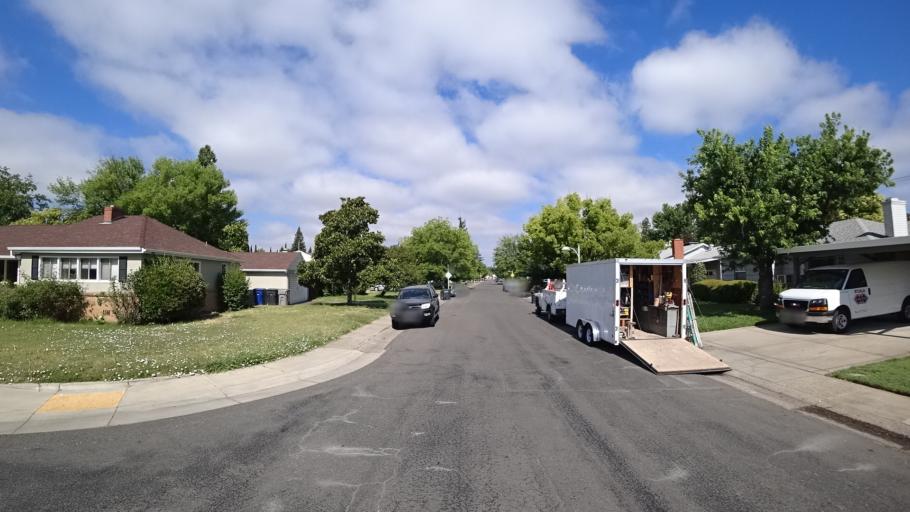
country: US
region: California
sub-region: Sacramento County
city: Parkway
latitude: 38.5337
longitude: -121.4885
